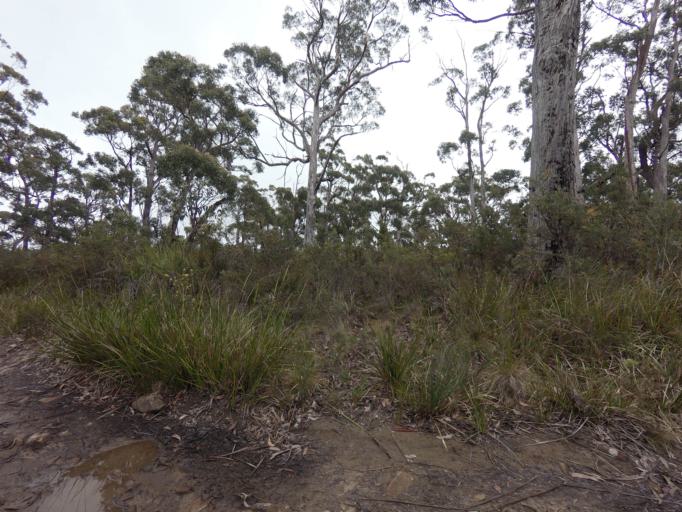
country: AU
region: Tasmania
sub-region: Huon Valley
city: Geeveston
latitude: -43.4711
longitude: 146.9322
